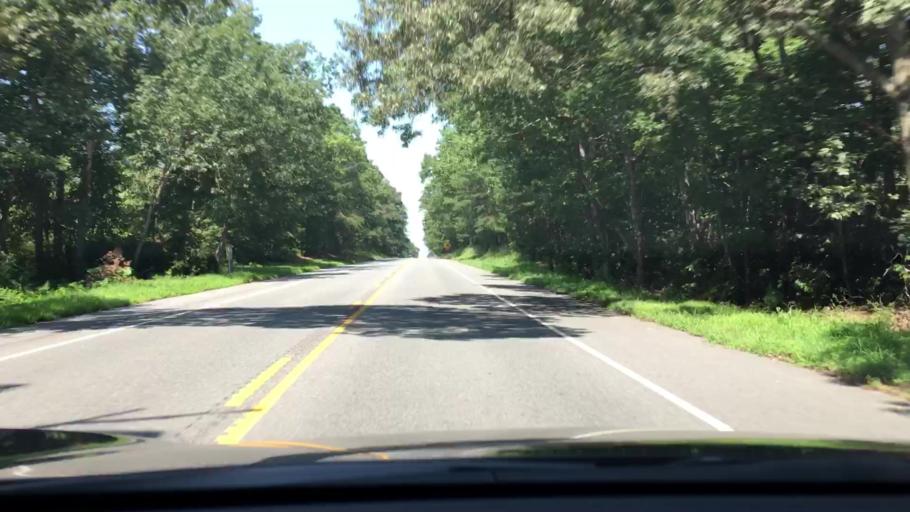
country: US
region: New Jersey
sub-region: Cumberland County
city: Laurel Lake
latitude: 39.3510
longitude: -75.0546
